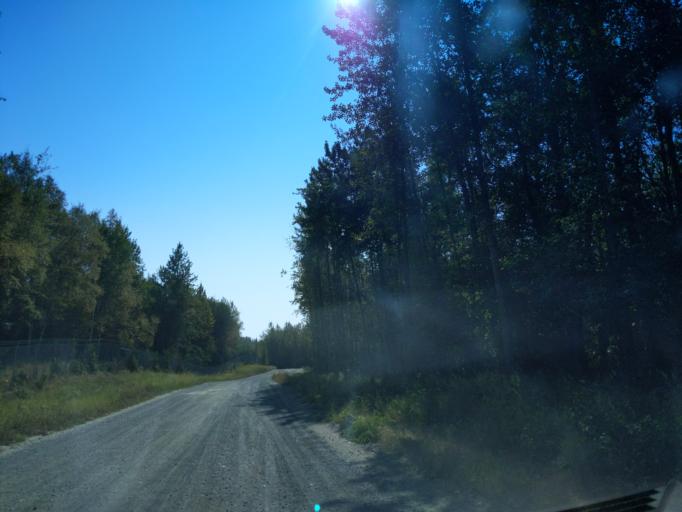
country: US
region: Alaska
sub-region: Anchorage Municipality
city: Anchorage
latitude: 61.1626
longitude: -150.0148
